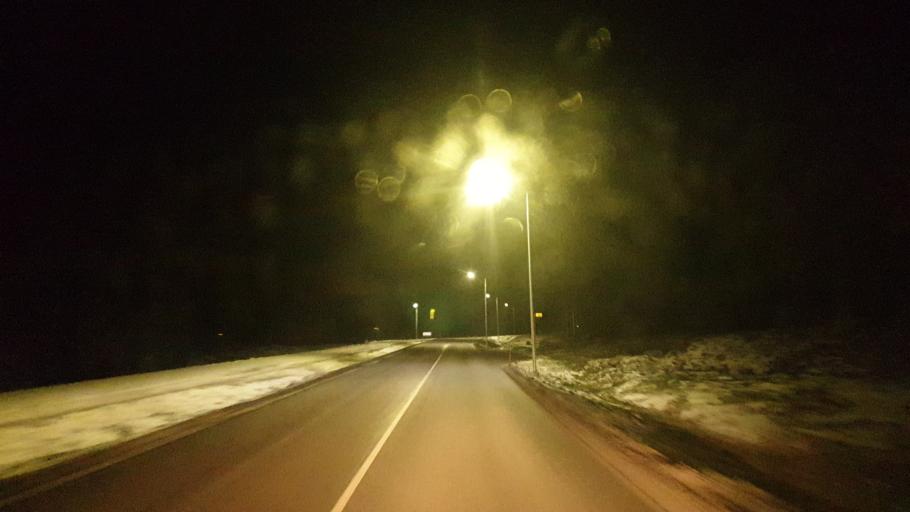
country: FI
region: Southern Savonia
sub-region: Pieksaemaeki
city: Juva
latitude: 61.8768
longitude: 27.7727
